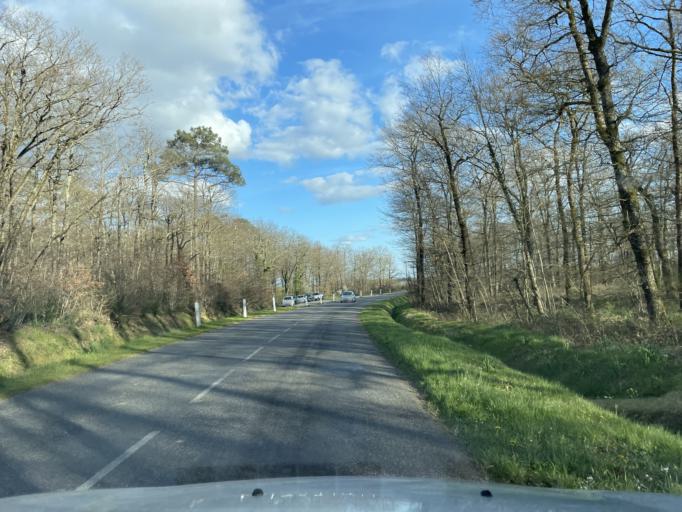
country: FR
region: Midi-Pyrenees
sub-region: Departement de la Haute-Garonne
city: Leguevin
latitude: 43.6140
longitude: 1.2042
